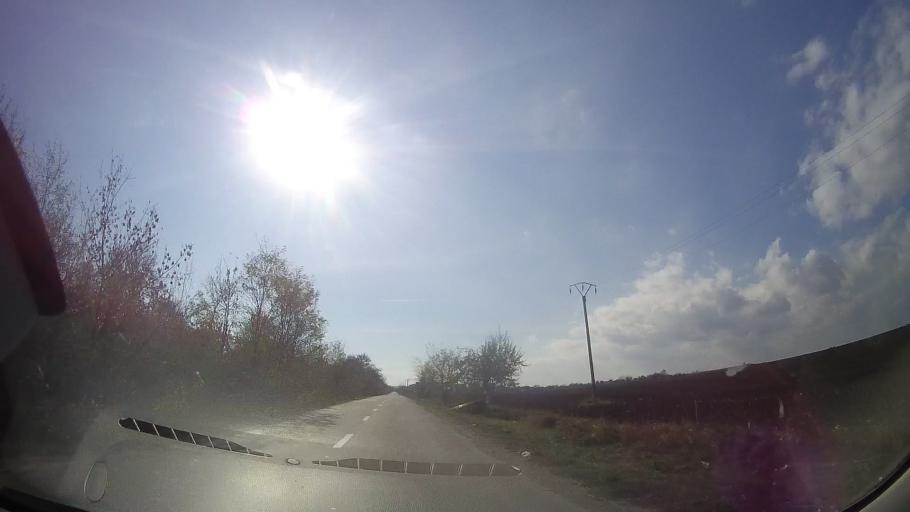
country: RO
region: Constanta
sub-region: Comuna Costinesti
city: Costinesti
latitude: 43.9610
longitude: 28.6363
